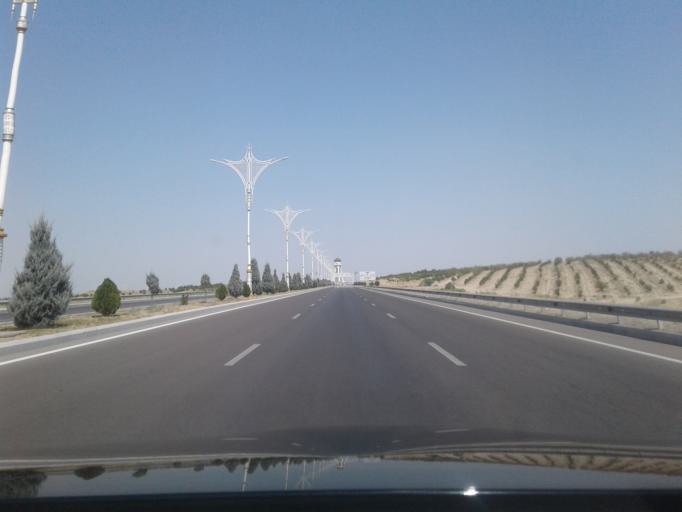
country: TM
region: Ahal
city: Ashgabat
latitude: 37.8782
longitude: 58.4130
